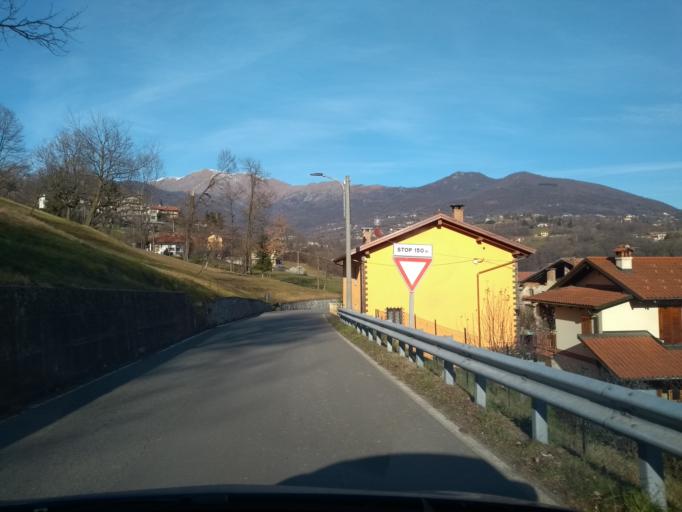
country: IT
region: Piedmont
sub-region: Provincia di Torino
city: Lanzo Torinese
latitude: 45.2805
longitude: 7.4683
